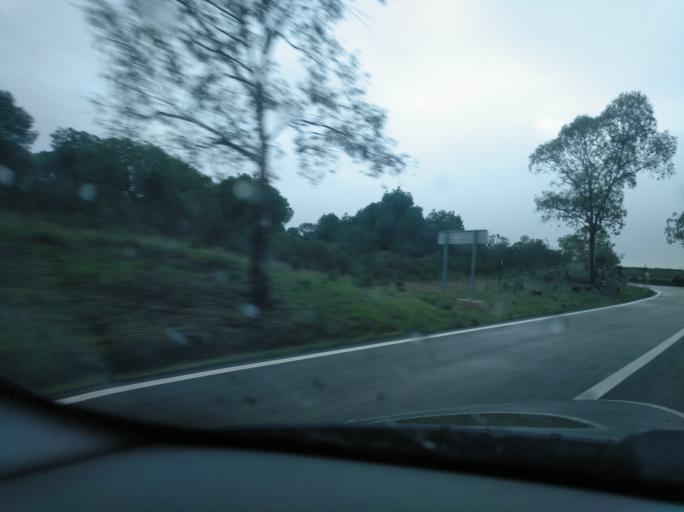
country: PT
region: Faro
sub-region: Alcoutim
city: Alcoutim
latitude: 37.4896
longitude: -7.5731
